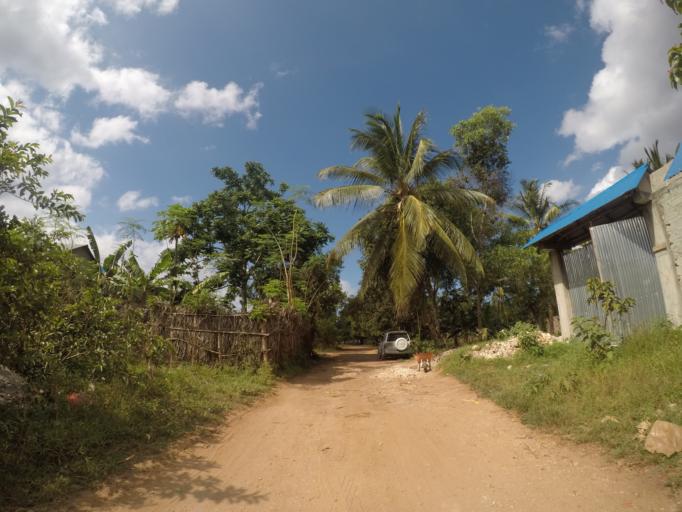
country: TZ
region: Zanzibar Central/South
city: Koani
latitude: -6.1963
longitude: 39.3162
